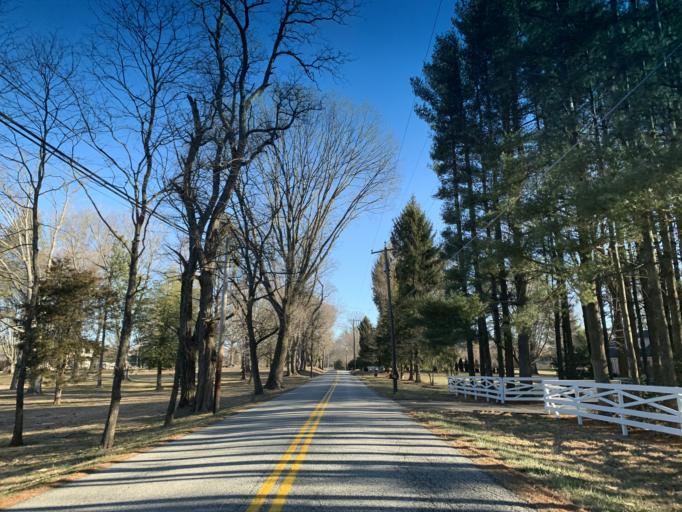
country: US
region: Maryland
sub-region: Harford County
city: Riverside
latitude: 39.5658
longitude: -76.2415
